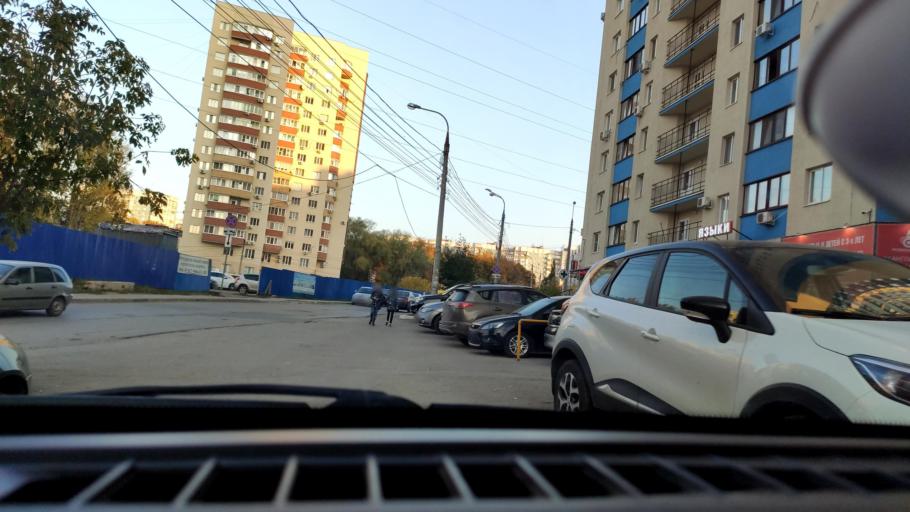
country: RU
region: Samara
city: Samara
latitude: 53.2434
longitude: 50.1875
